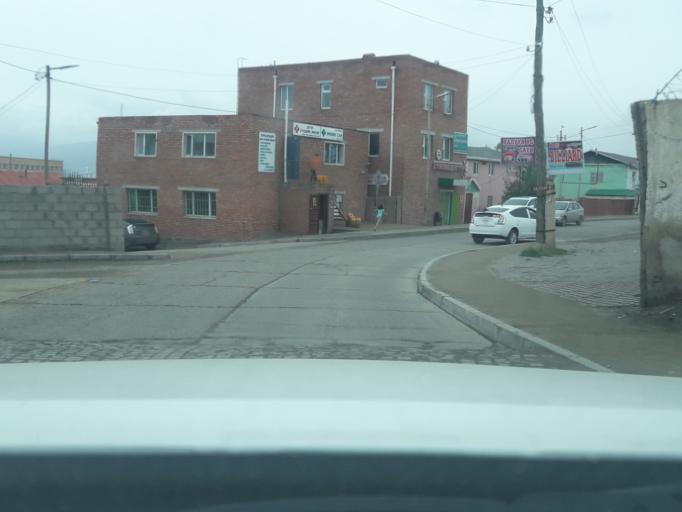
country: MN
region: Ulaanbaatar
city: Ulaanbaatar
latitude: 47.9471
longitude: 106.9035
